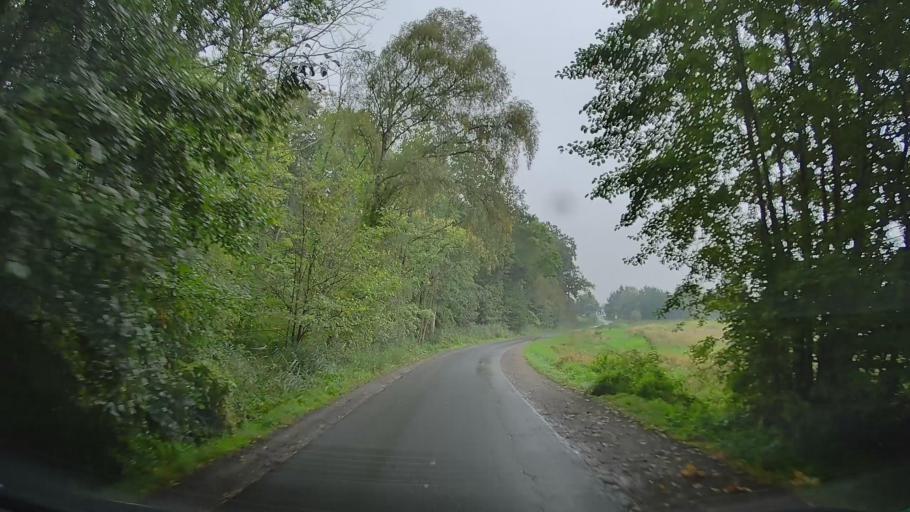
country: DE
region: Mecklenburg-Vorpommern
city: Gramkow
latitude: 53.9284
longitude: 11.3655
